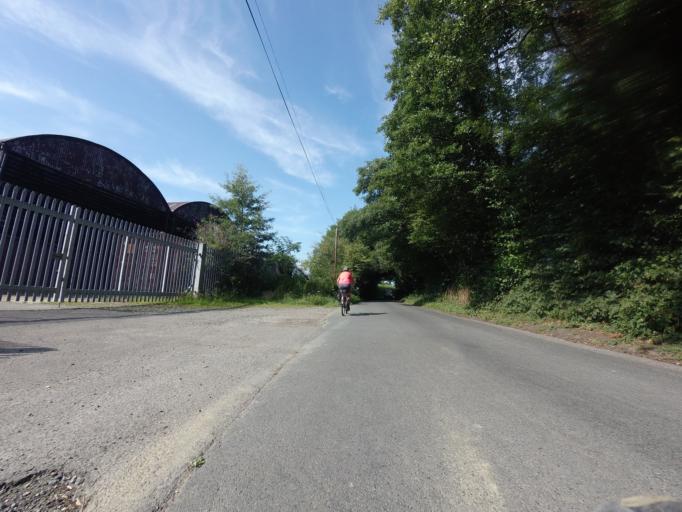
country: GB
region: England
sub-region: East Sussex
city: Rye
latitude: 50.9896
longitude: 0.6765
